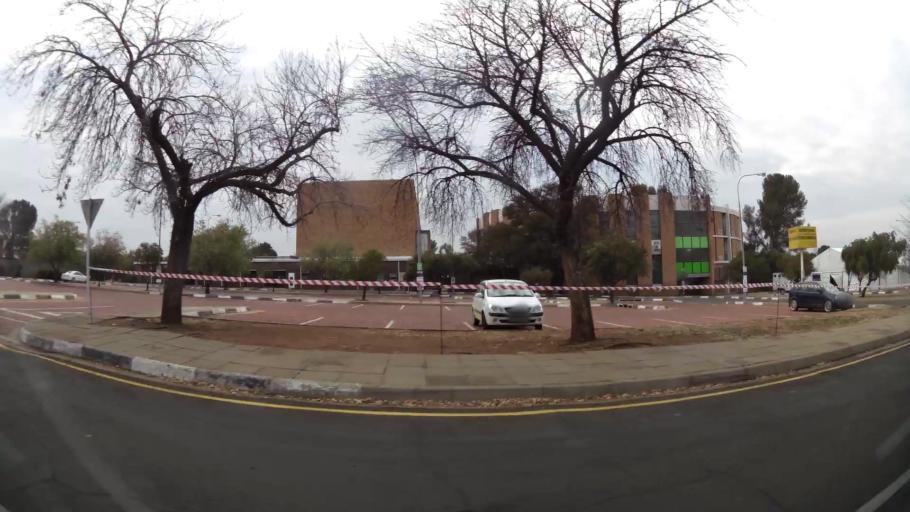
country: ZA
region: Orange Free State
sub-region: Mangaung Metropolitan Municipality
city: Bloemfontein
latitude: -29.1108
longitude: 26.1901
